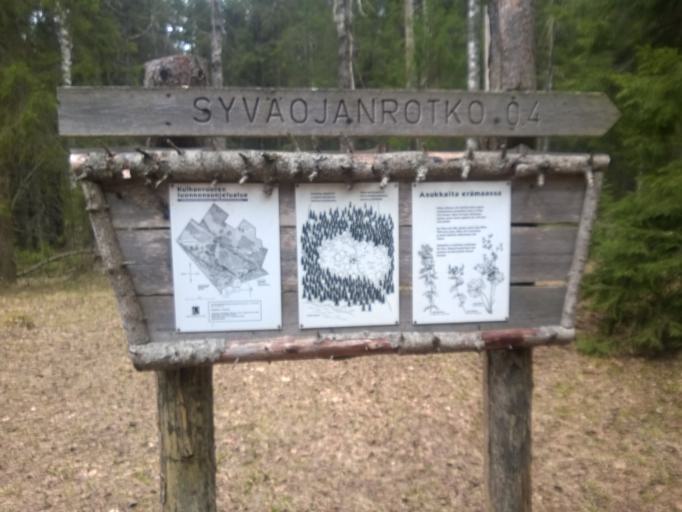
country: FI
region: Central Finland
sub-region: Saarijaervi-Viitasaari
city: Pylkoenmaeki
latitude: 62.5812
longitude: 24.9708
